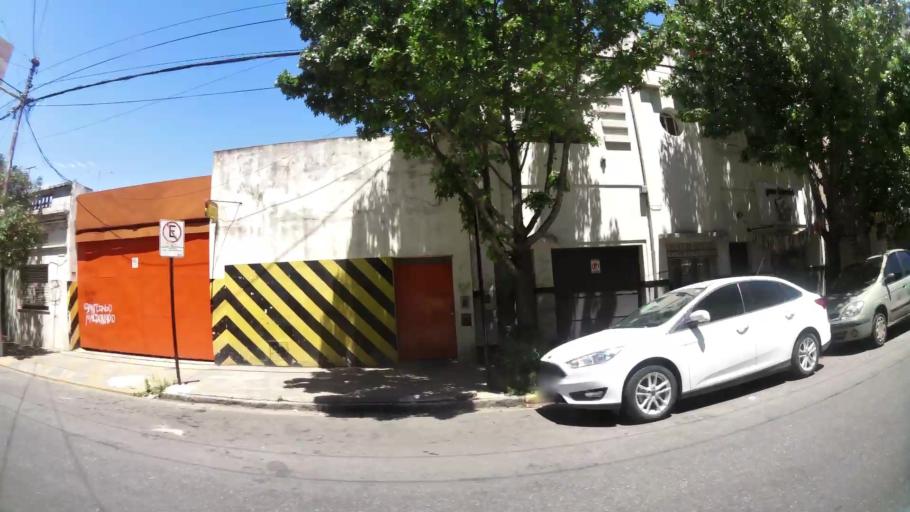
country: AR
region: Santa Fe
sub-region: Departamento de Rosario
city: Rosario
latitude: -32.9473
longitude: -60.6637
